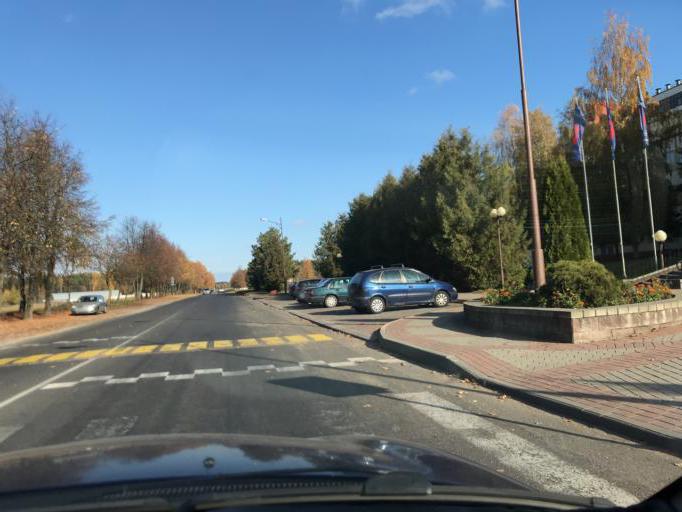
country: BY
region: Grodnenskaya
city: Lida
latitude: 53.9403
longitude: 25.2454
